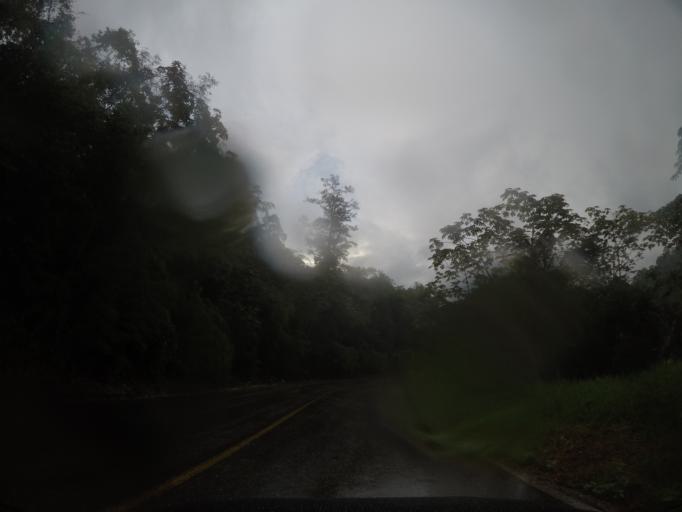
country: MX
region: Oaxaca
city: San Gabriel Mixtepec
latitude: 16.0828
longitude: -97.0799
